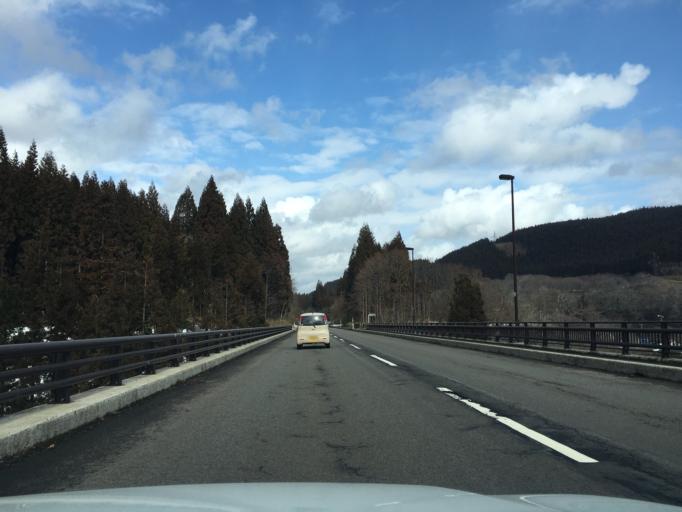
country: JP
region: Akita
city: Takanosu
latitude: 40.0094
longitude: 140.2787
